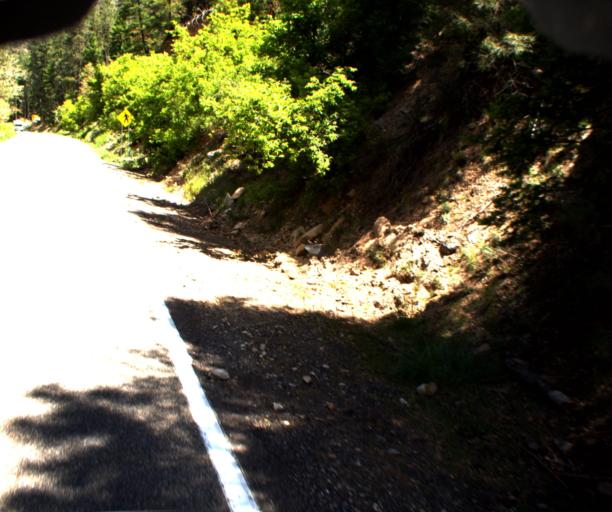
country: US
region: Arizona
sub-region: Coconino County
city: Sedona
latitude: 34.9743
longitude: -111.7470
